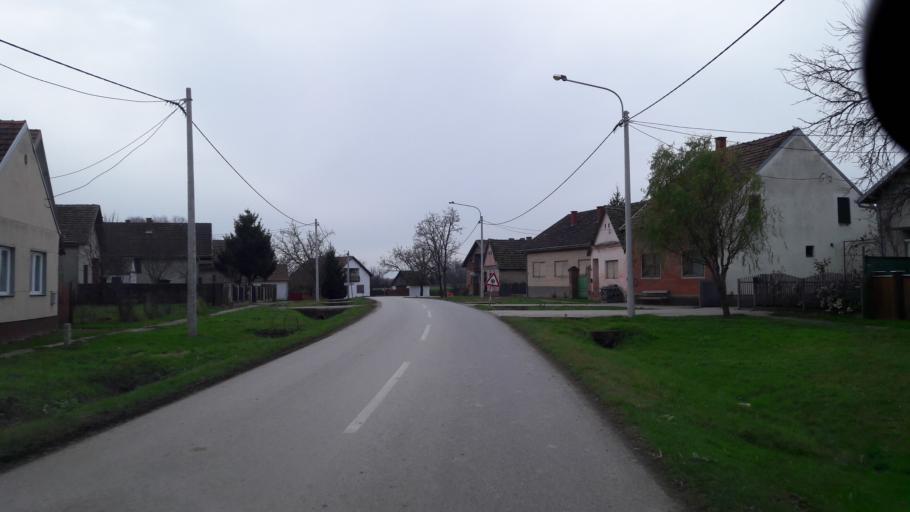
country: HR
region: Osjecko-Baranjska
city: Vladislavci
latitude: 45.4320
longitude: 18.5961
